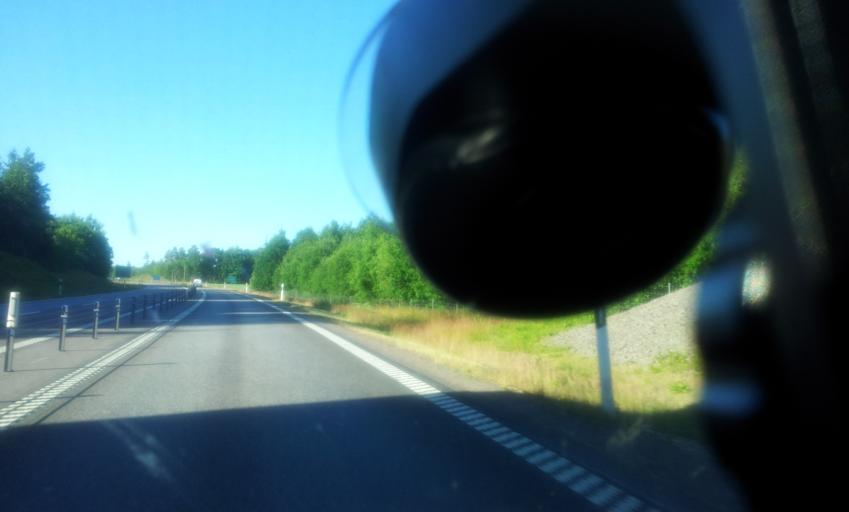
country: SE
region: Kalmar
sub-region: Kalmar Kommun
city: Ljungbyholm
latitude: 56.5640
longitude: 16.0892
